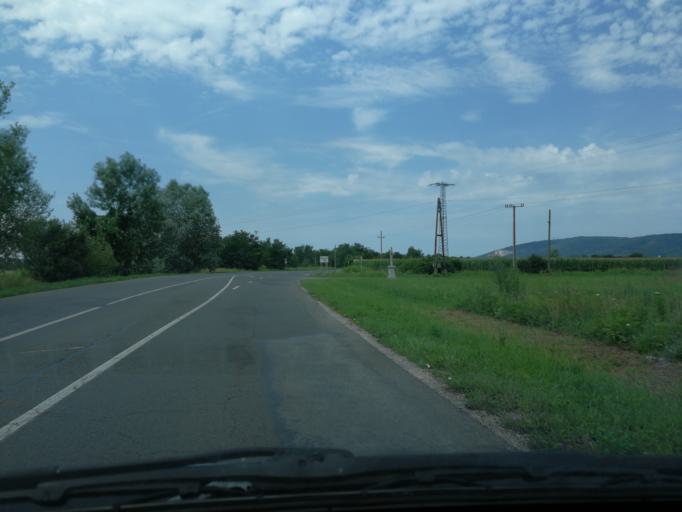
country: HU
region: Baranya
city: Siklos
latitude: 45.8515
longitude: 18.3224
